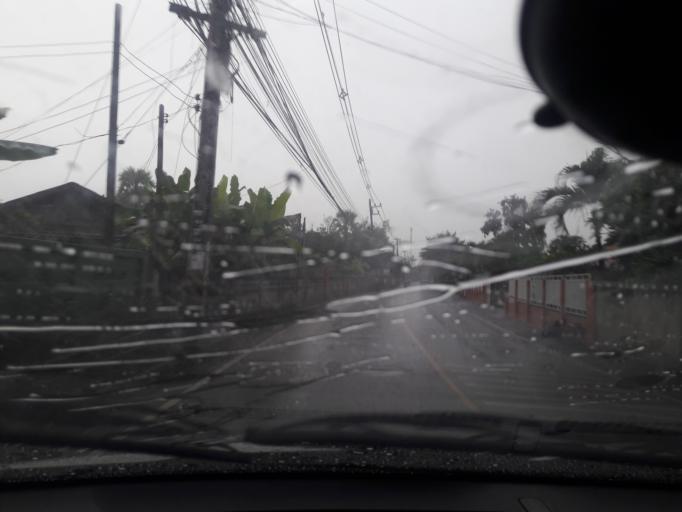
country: TH
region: Chiang Mai
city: San Kamphaeng
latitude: 18.7588
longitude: 99.1389
